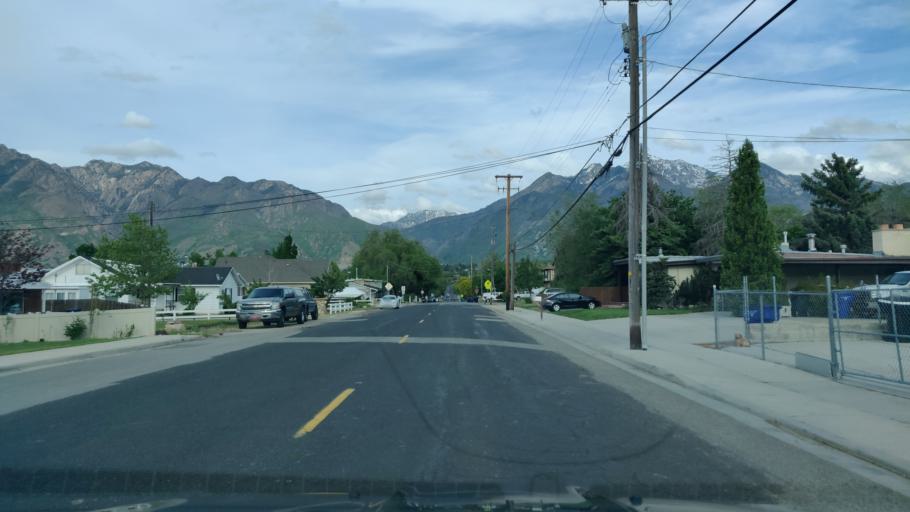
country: US
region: Utah
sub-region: Salt Lake County
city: Little Cottonwood Creek Valley
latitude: 40.6204
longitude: -111.8455
